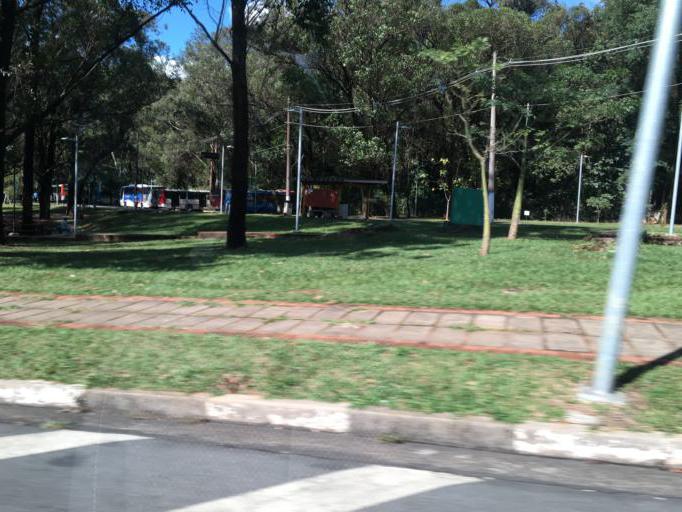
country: BR
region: Sao Paulo
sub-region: Osasco
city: Osasco
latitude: -23.5593
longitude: -46.7381
